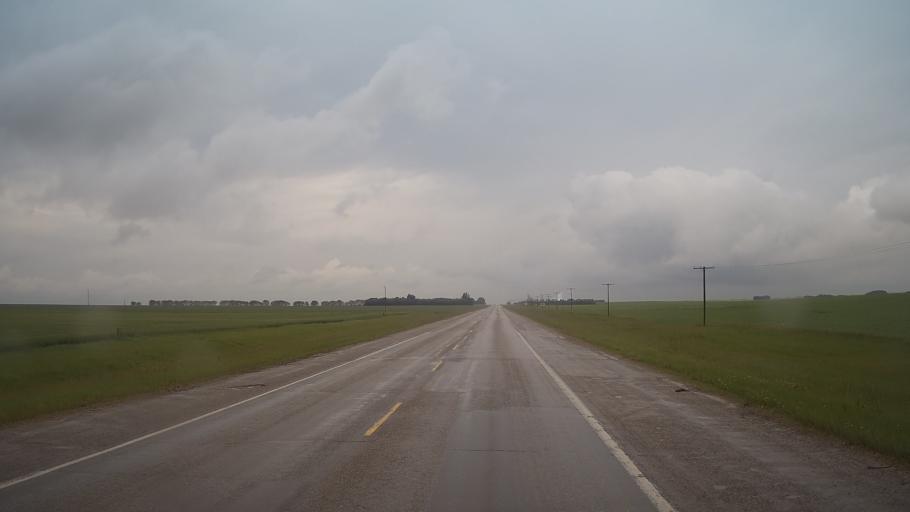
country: CA
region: Saskatchewan
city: Unity
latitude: 52.4350
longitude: -109.0696
